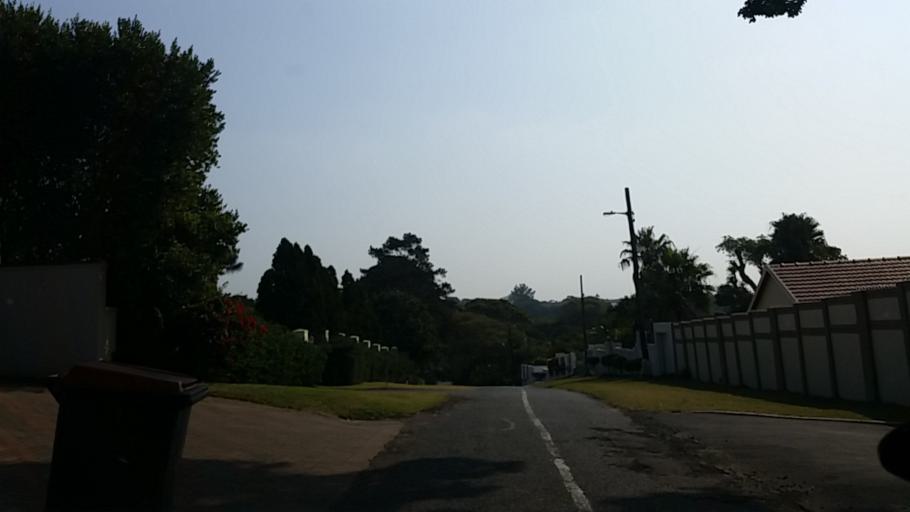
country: ZA
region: KwaZulu-Natal
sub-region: eThekwini Metropolitan Municipality
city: Berea
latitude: -29.8348
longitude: 30.9338
